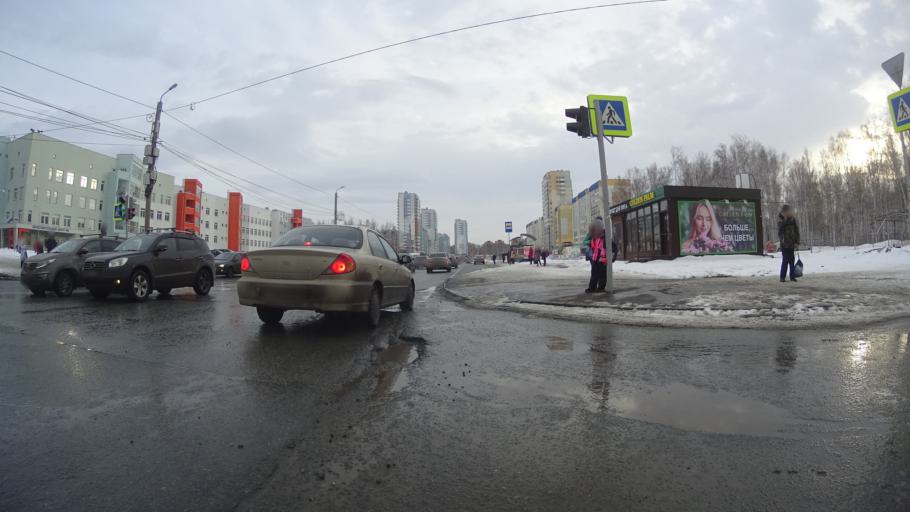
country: RU
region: Chelyabinsk
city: Roshchino
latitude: 55.2073
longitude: 61.2842
